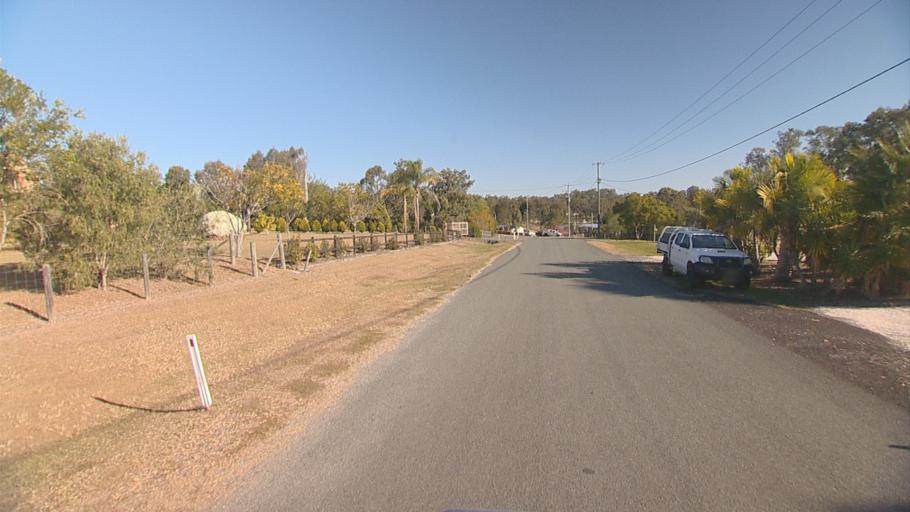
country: AU
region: Queensland
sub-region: Logan
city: North Maclean
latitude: -27.7892
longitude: 153.0248
